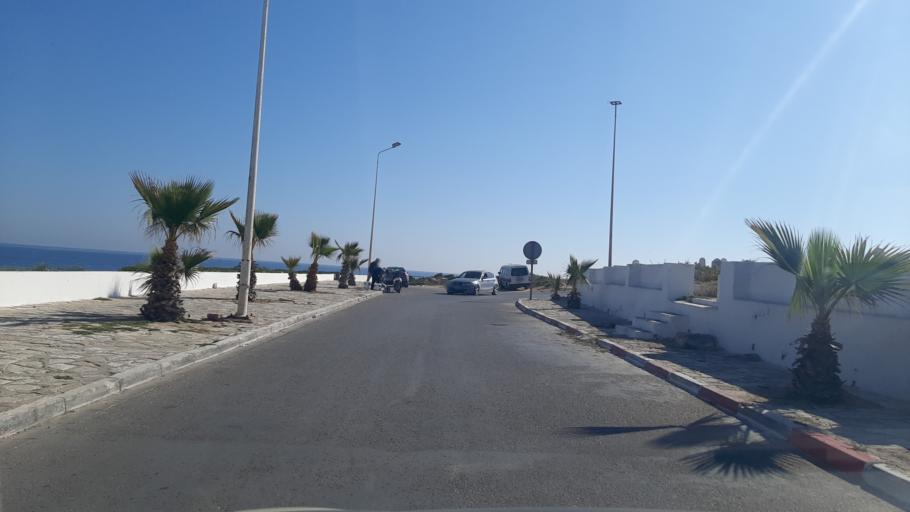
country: TN
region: Al Mahdiyah
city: Mahdia
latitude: 35.5085
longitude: 11.0794
